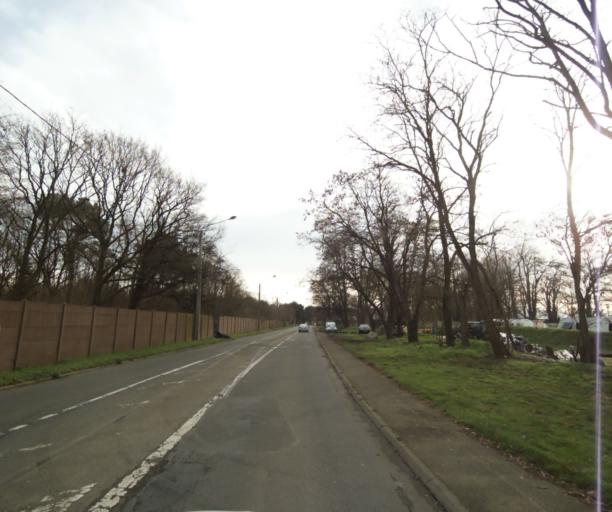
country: FR
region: Pays de la Loire
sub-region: Departement de la Sarthe
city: Arnage
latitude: 47.9523
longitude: 0.1873
